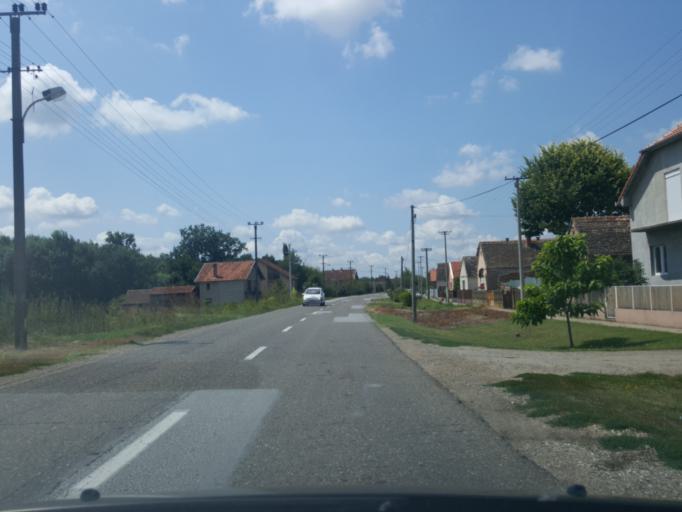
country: RS
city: Salas Nocajski
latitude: 44.9306
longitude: 19.5647
